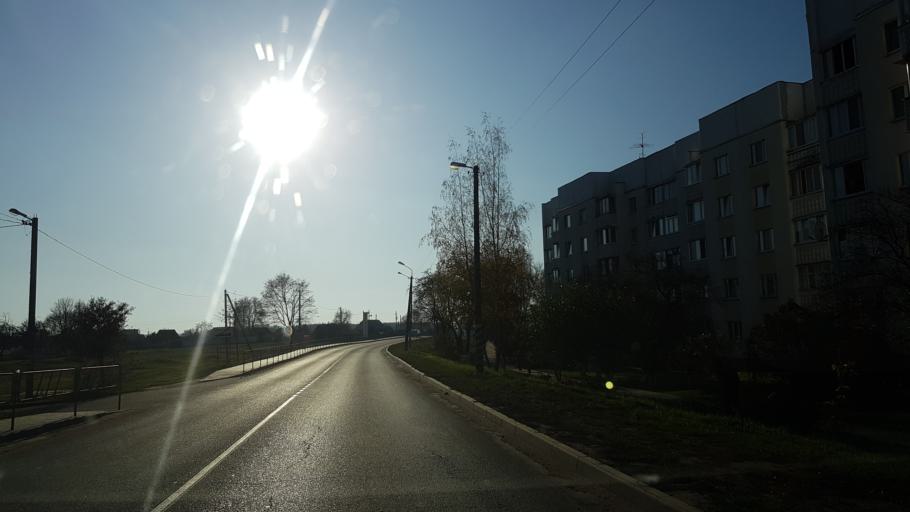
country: BY
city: Fanipol
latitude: 53.7390
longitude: 27.3144
